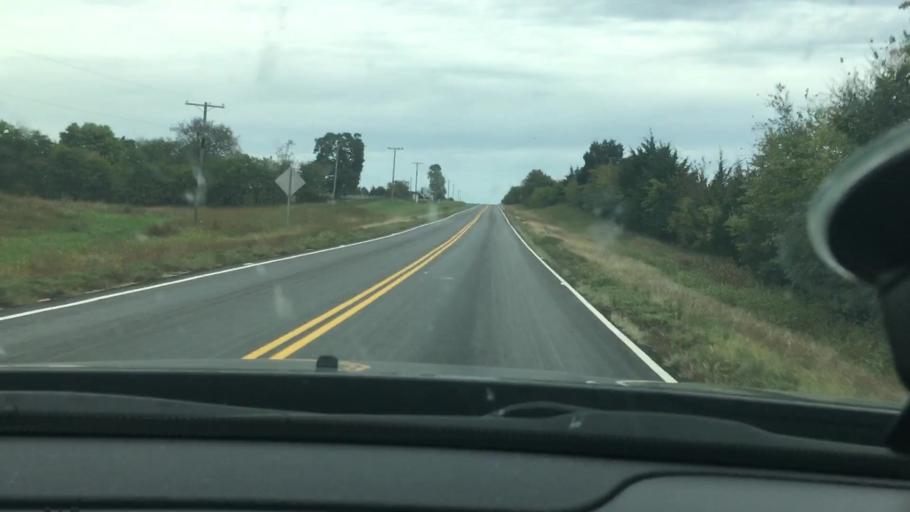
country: US
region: Oklahoma
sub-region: Coal County
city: Coalgate
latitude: 34.3864
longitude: -96.4245
